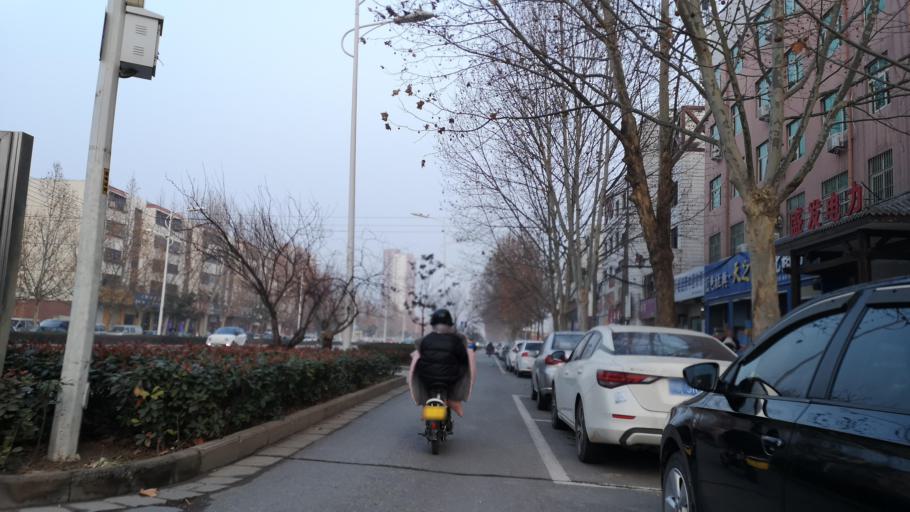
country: CN
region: Henan Sheng
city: Puyang
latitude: 35.7487
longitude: 115.0313
